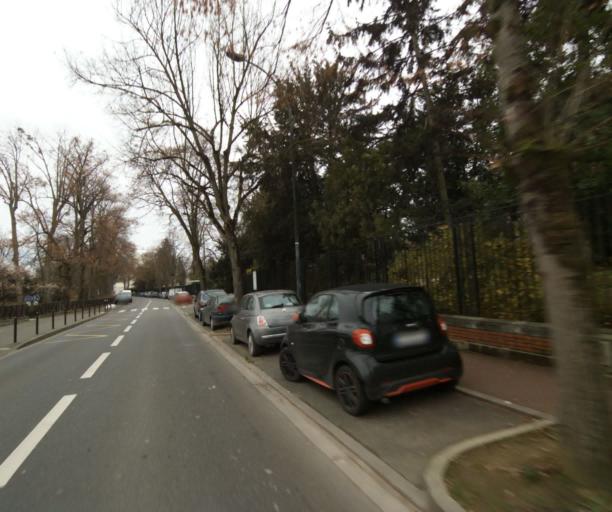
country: FR
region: Ile-de-France
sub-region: Departement des Hauts-de-Seine
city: Saint-Cloud
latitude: 48.8538
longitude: 2.2000
